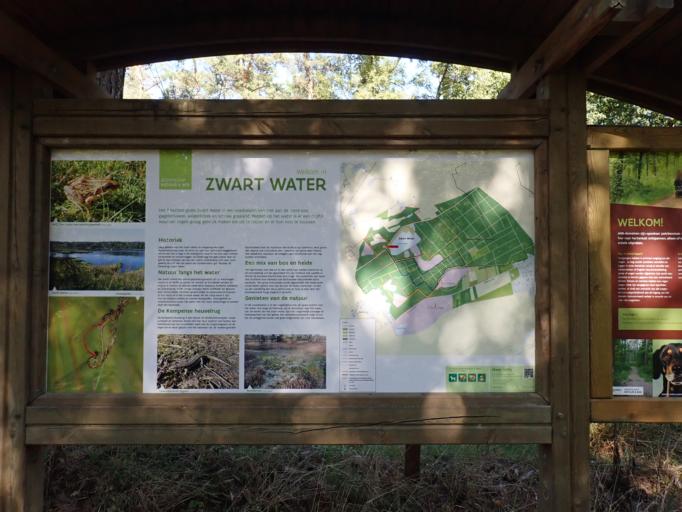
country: BE
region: Flanders
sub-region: Provincie Antwerpen
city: Herentals
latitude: 51.2100
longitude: 4.8730
